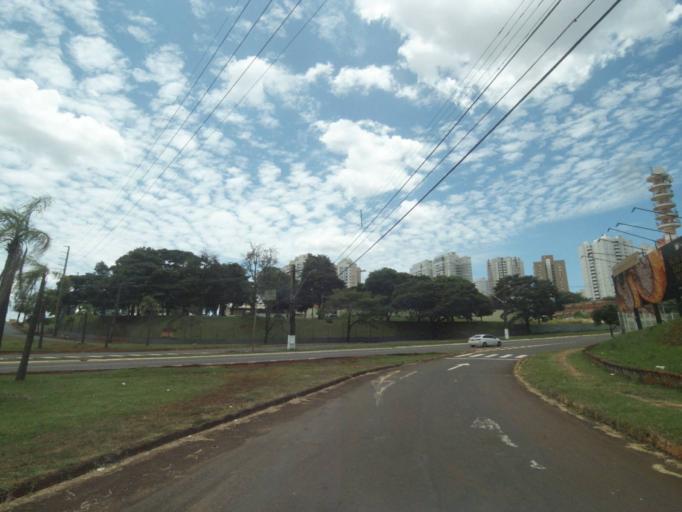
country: BR
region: Parana
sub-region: Londrina
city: Londrina
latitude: -23.3371
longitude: -51.1835
